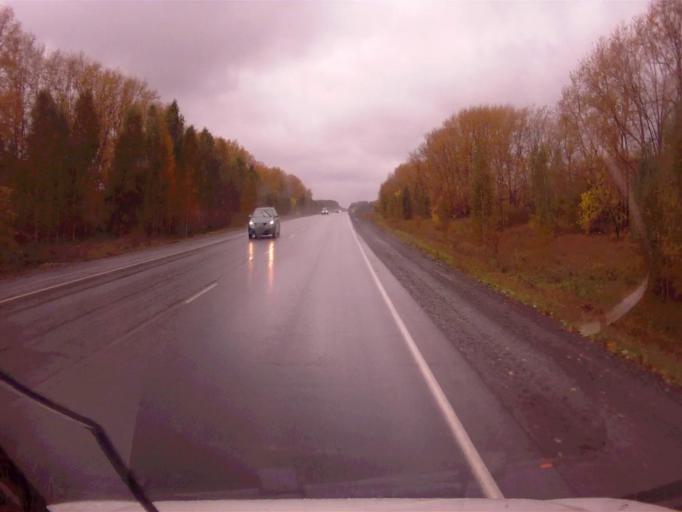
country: RU
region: Chelyabinsk
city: Argayash
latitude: 55.4516
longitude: 60.9353
